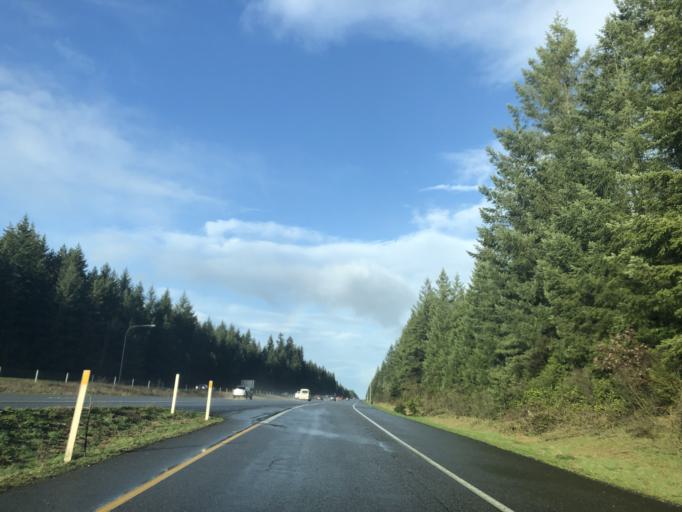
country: US
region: Washington
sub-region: Kitsap County
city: Bangor Trident Base
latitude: 47.7045
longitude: -122.6834
